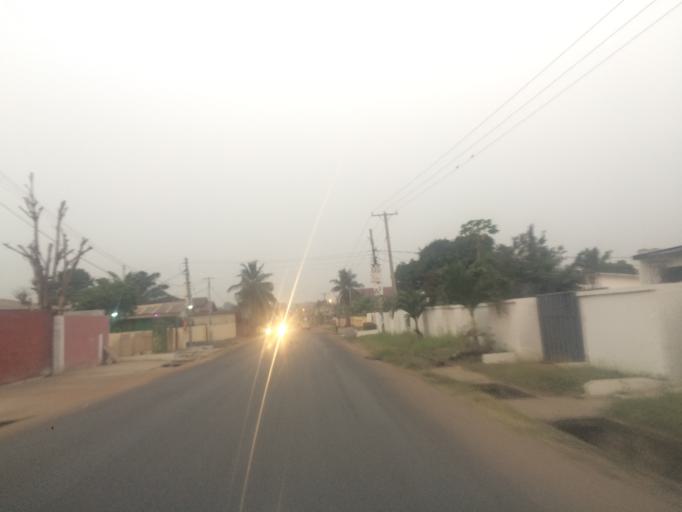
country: GH
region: Greater Accra
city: Nungua
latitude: 5.6015
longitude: -0.0922
